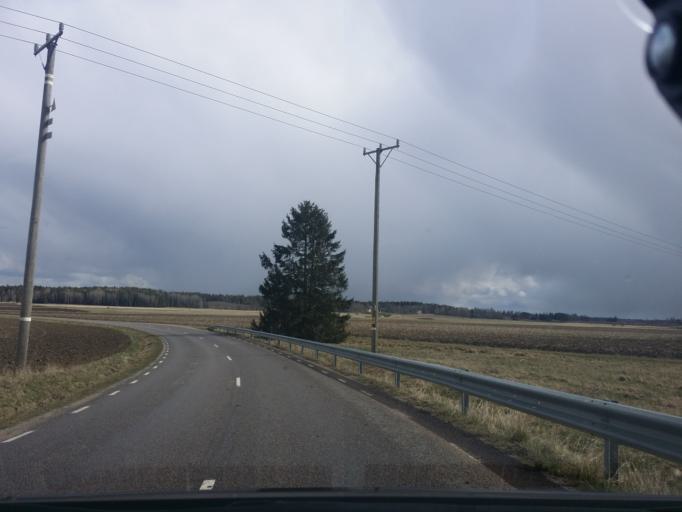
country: SE
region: Vaestmanland
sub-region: Sala Kommun
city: Sala
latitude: 59.9106
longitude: 16.6344
